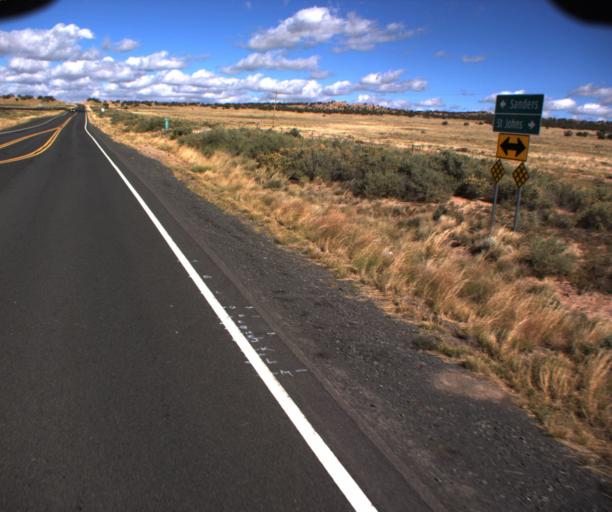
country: US
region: Arizona
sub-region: Apache County
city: Houck
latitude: 35.0635
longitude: -109.2819
